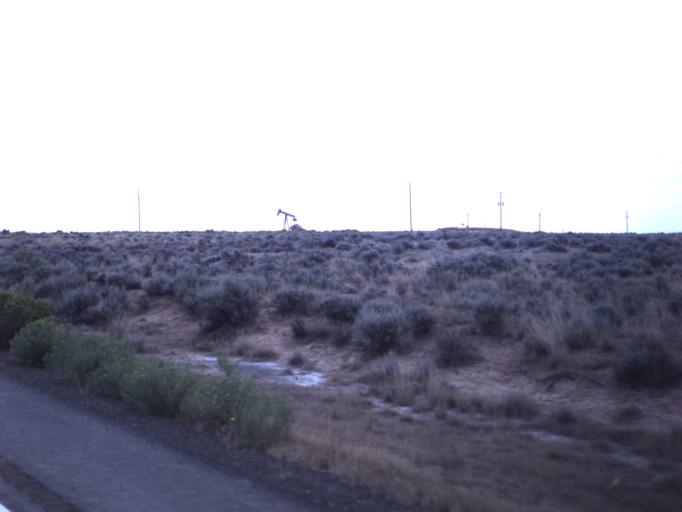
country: US
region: Utah
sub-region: Uintah County
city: Naples
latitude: 40.2058
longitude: -109.3591
